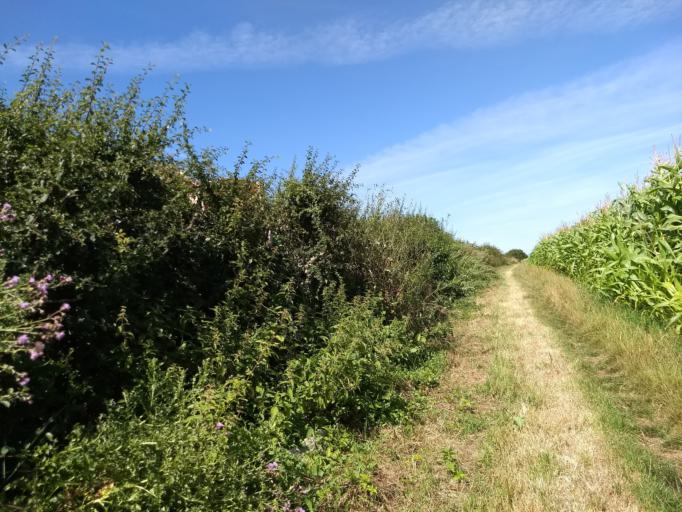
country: GB
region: England
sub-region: Isle of Wight
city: Brading
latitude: 50.6965
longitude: -1.1596
